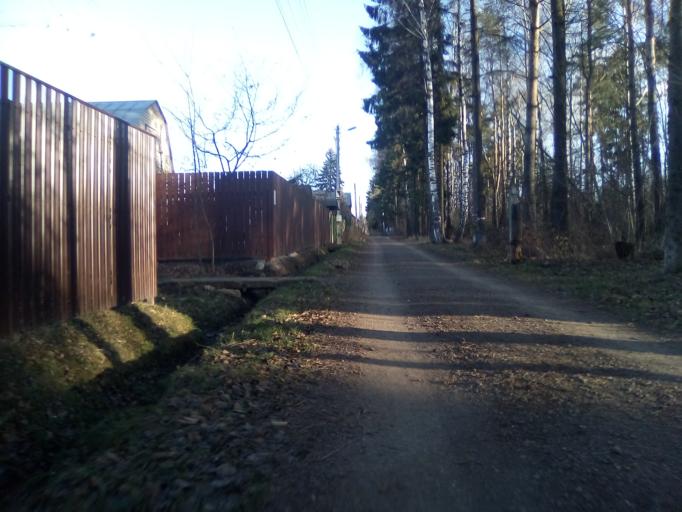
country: RU
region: Moskovskaya
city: Lesnoy Gorodok
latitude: 55.6648
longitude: 37.1996
